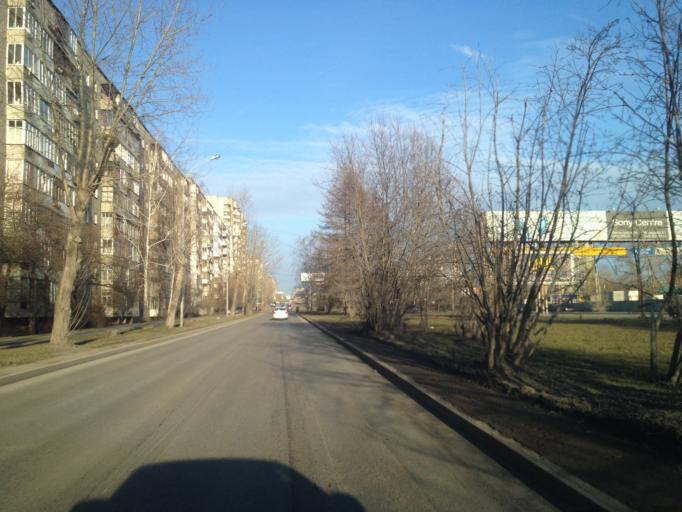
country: RU
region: Sverdlovsk
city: Shirokaya Rechka
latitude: 56.8271
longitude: 60.5375
